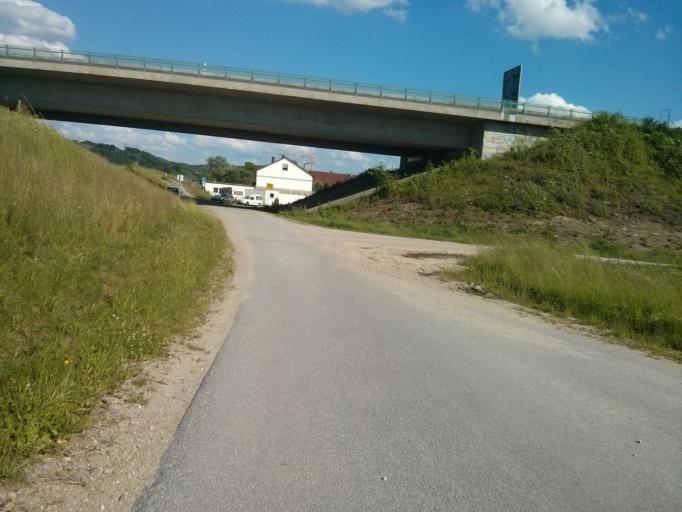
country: DE
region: Bavaria
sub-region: Lower Bavaria
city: Deggendorf
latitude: 48.8262
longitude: 12.9457
